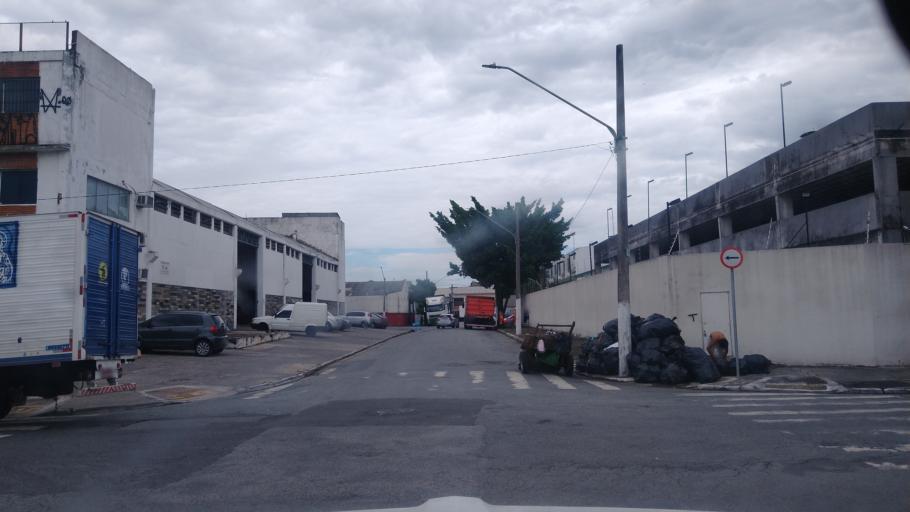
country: BR
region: Sao Paulo
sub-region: Guarulhos
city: Guarulhos
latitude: -23.5140
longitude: -46.5687
